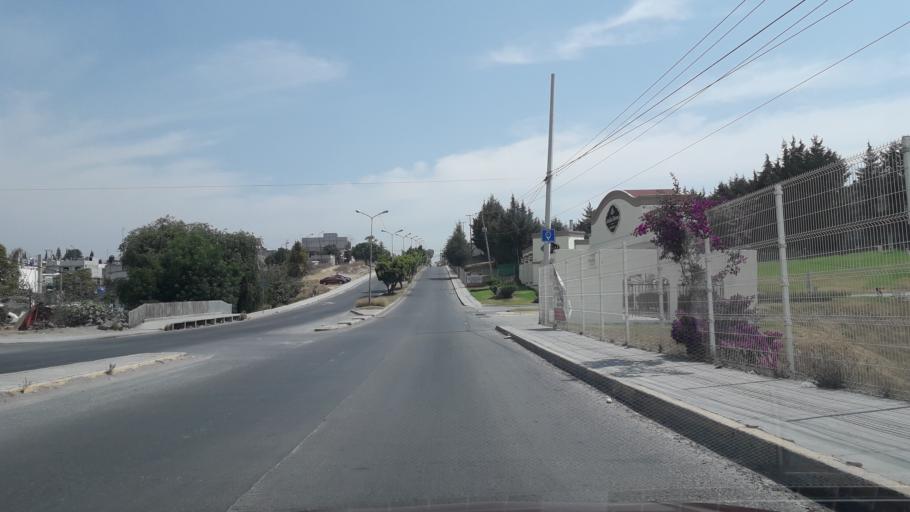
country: MX
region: Puebla
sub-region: Puebla
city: El Capulo (La Quebradora)
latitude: 18.9580
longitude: -98.2685
